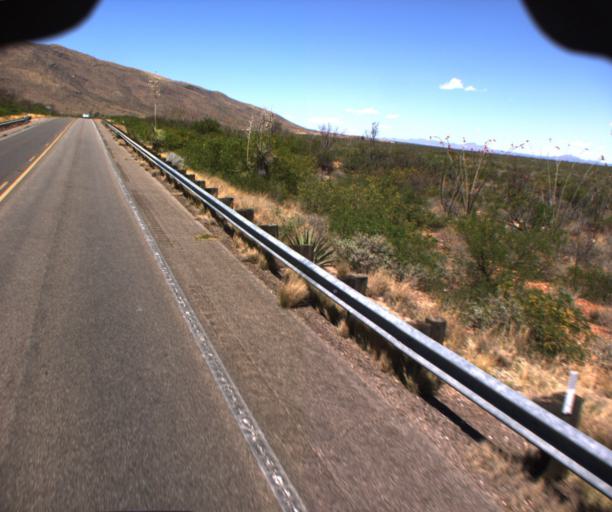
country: US
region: Arizona
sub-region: Cochise County
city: Bisbee
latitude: 31.4325
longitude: -109.8125
